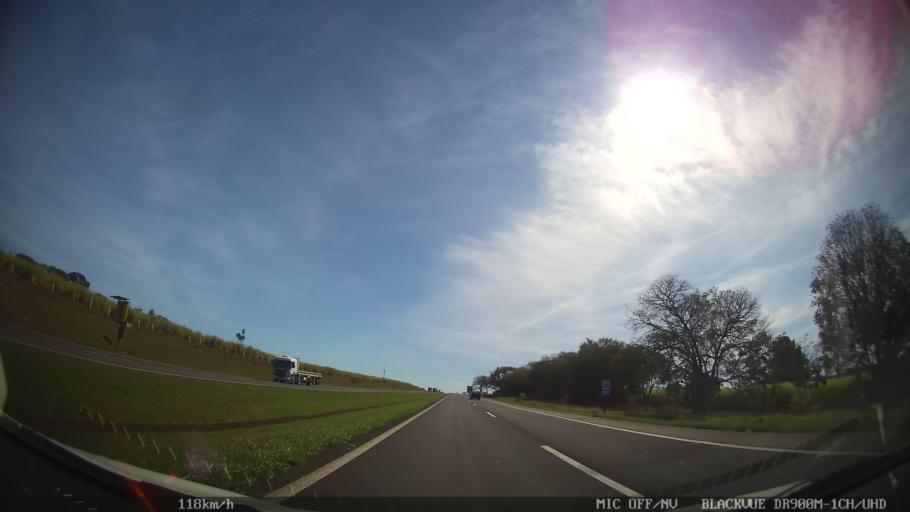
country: BR
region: Sao Paulo
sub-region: Leme
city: Leme
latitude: -22.1143
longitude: -47.4118
